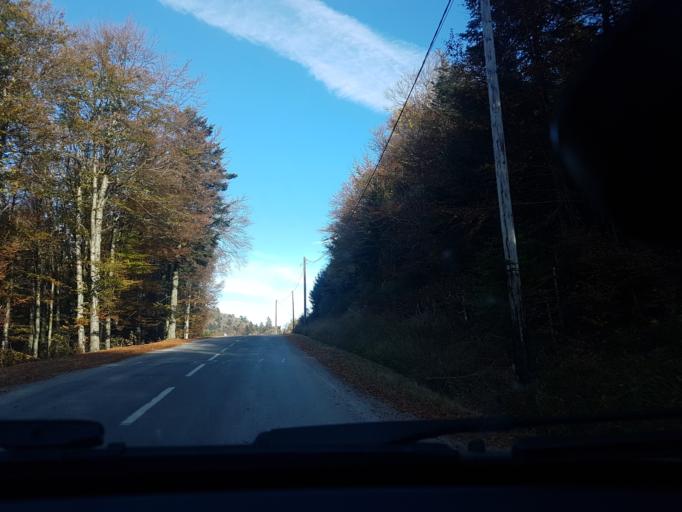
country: FR
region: Franche-Comte
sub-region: Departement de la Haute-Saone
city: Plancher-les-Mines
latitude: 47.7735
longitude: 6.7766
